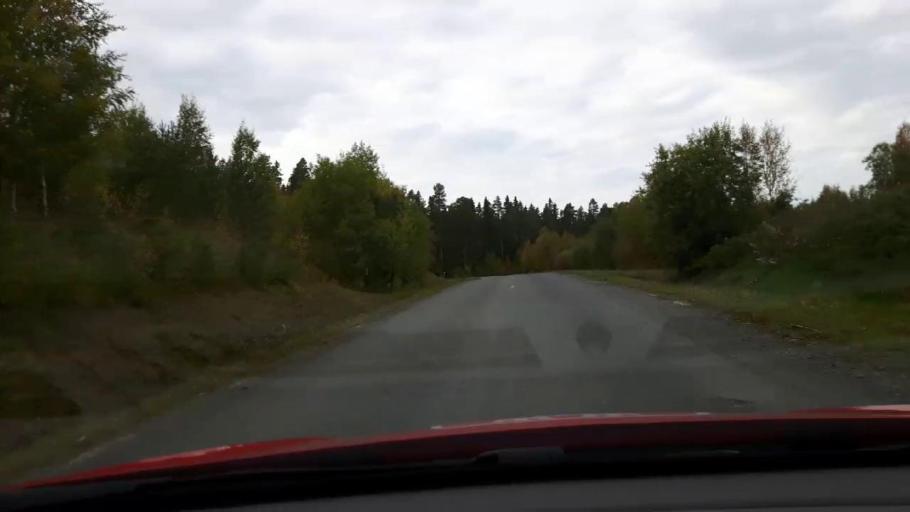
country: SE
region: Jaemtland
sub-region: Krokoms Kommun
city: Krokom
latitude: 63.2029
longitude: 14.1182
